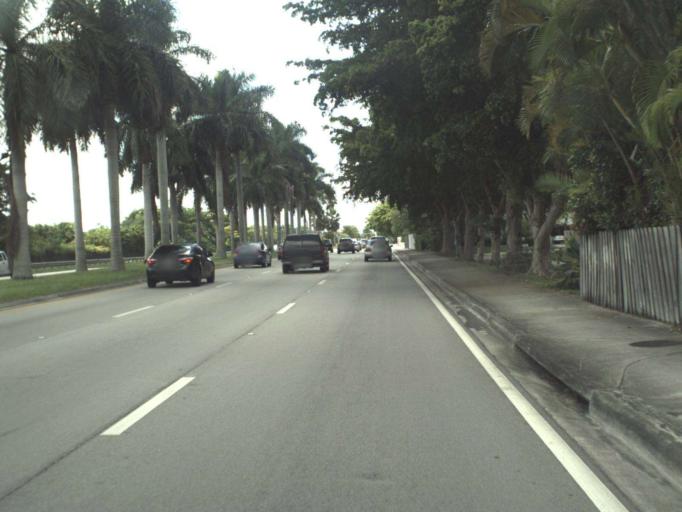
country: US
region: Florida
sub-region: Miami-Dade County
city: The Crossings
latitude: 25.6688
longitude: -80.4164
